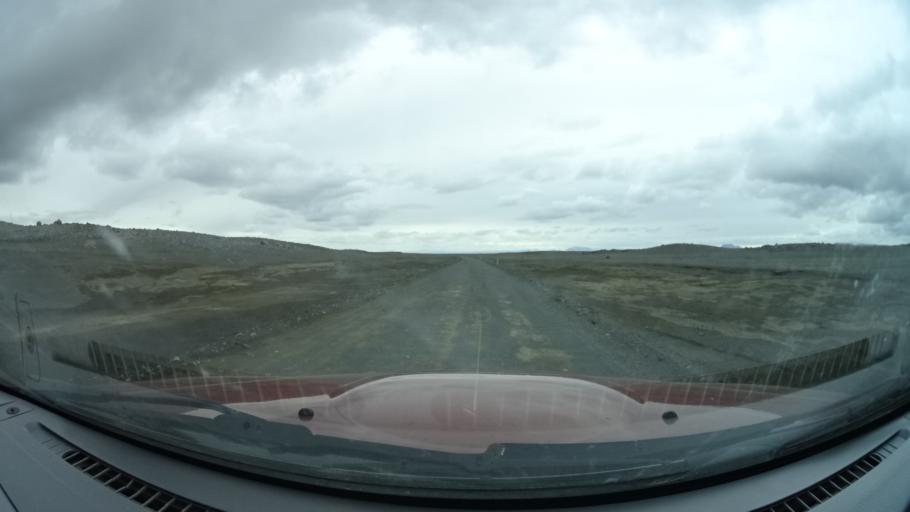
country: IS
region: Northeast
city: Husavik
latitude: 65.8051
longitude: -16.3491
